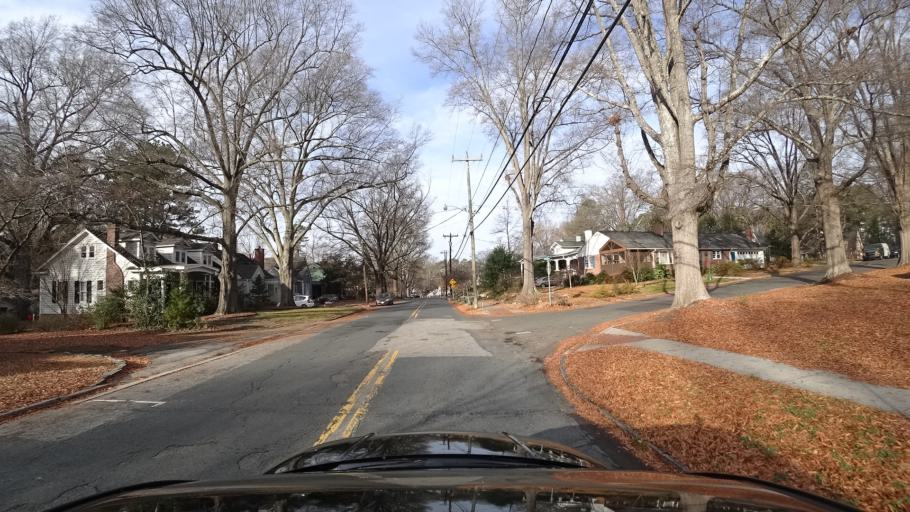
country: US
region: North Carolina
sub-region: Durham County
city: Durham
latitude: 36.0099
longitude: -78.8942
